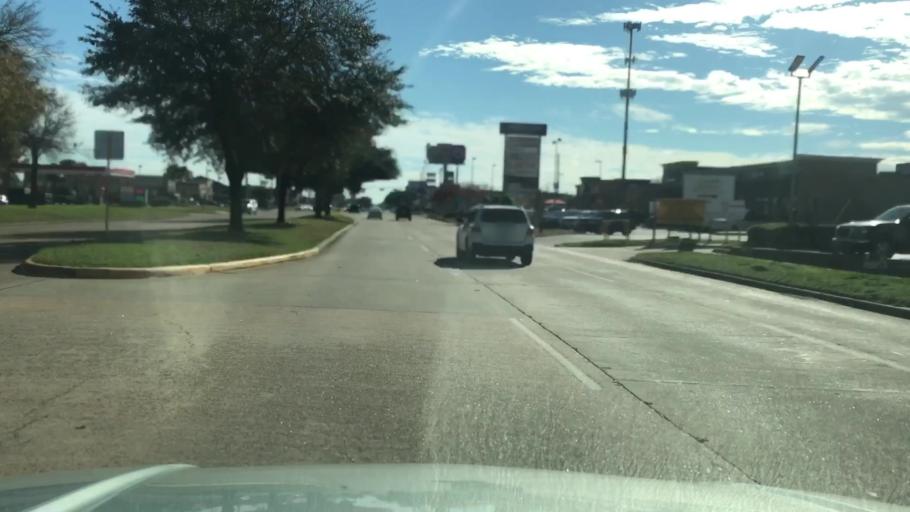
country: US
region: Texas
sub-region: Fort Bend County
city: Cinco Ranch
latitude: 29.7763
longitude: -95.7518
